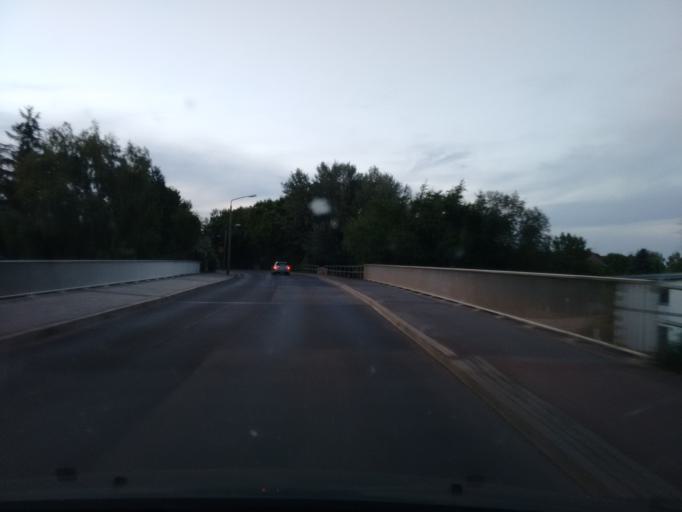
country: DE
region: Brandenburg
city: Storkow
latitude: 52.2570
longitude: 13.9363
